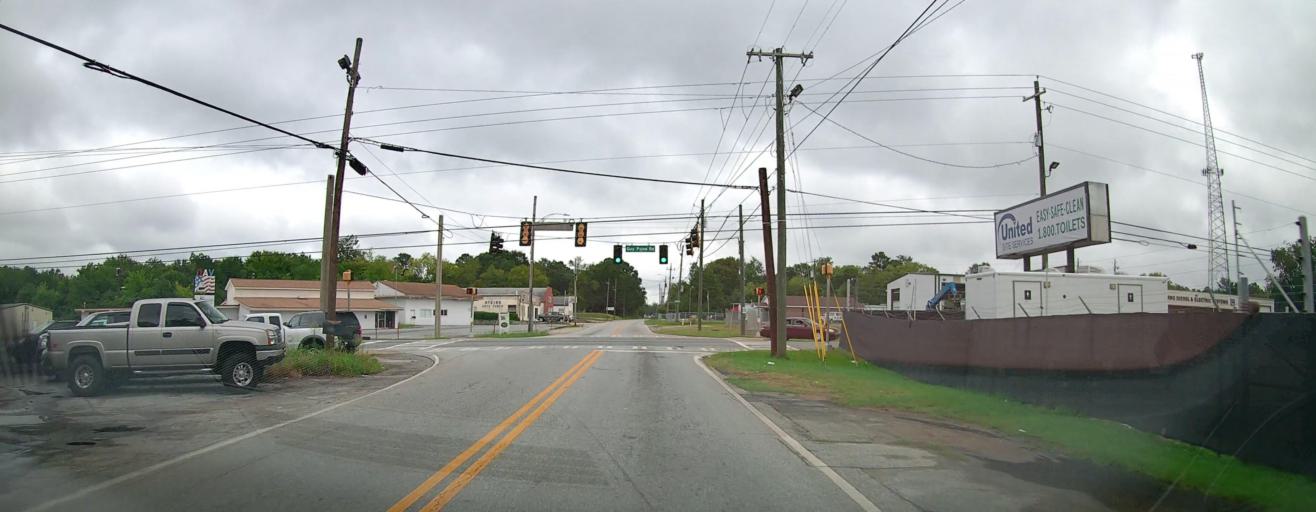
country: US
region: Georgia
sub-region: Bibb County
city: Macon
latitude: 32.7801
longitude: -83.6590
